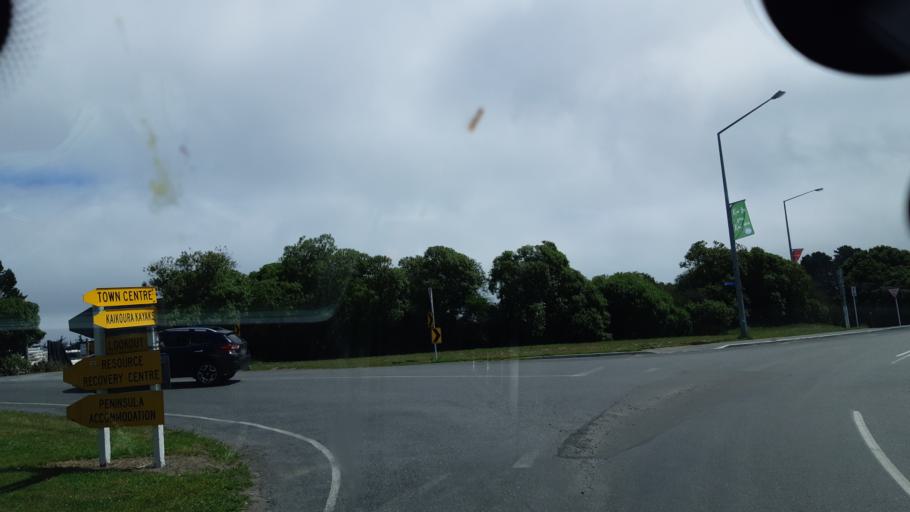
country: NZ
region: Canterbury
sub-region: Kaikoura District
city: Kaikoura
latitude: -42.4097
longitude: 173.6793
